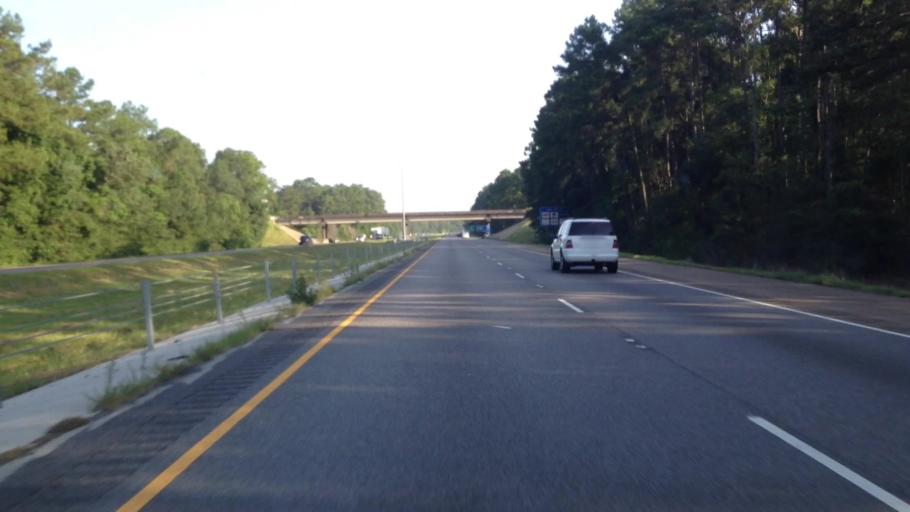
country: US
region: Louisiana
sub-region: Tangipahoa Parish
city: Hammond
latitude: 30.4895
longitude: -90.4964
